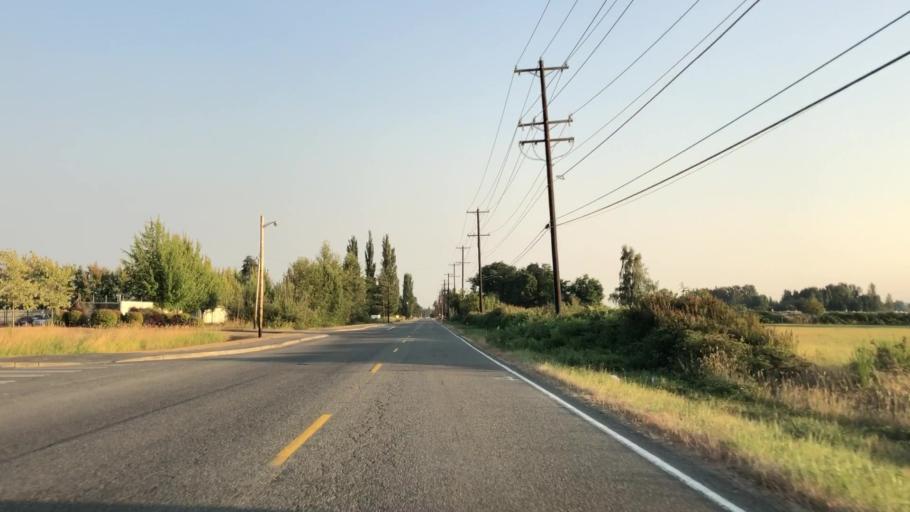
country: US
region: Washington
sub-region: Snohomish County
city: Smokey Point
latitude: 48.1481
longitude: -122.1616
